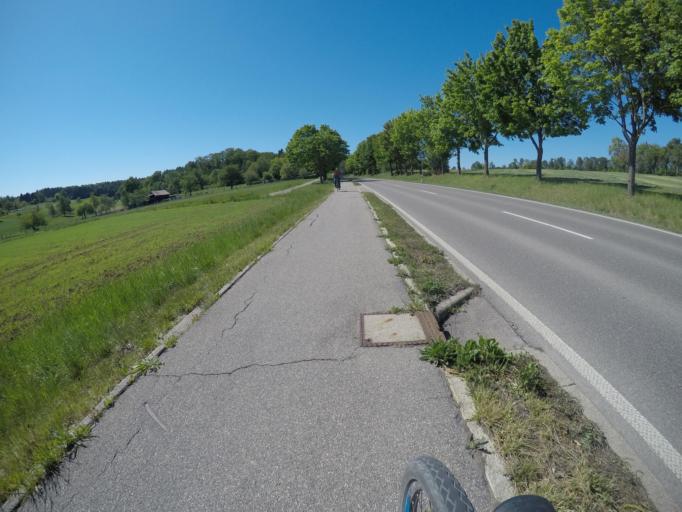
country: DE
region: Baden-Wuerttemberg
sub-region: Regierungsbezirk Stuttgart
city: Rutesheim
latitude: 48.8187
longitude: 8.9359
